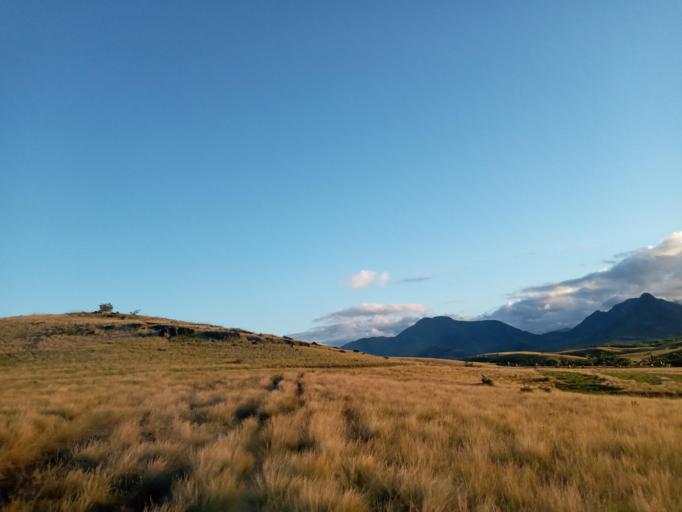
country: MG
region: Anosy
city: Fort Dauphin
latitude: -24.5126
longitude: 47.2521
